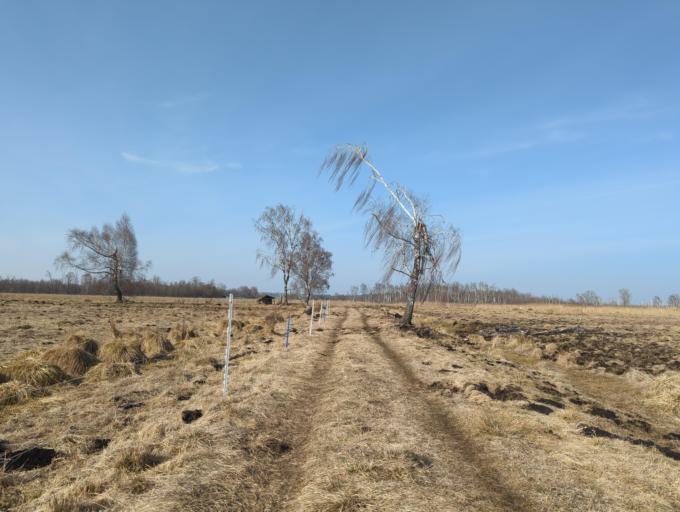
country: DE
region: Bavaria
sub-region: Swabia
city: Leipheim
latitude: 48.4838
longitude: 10.2142
